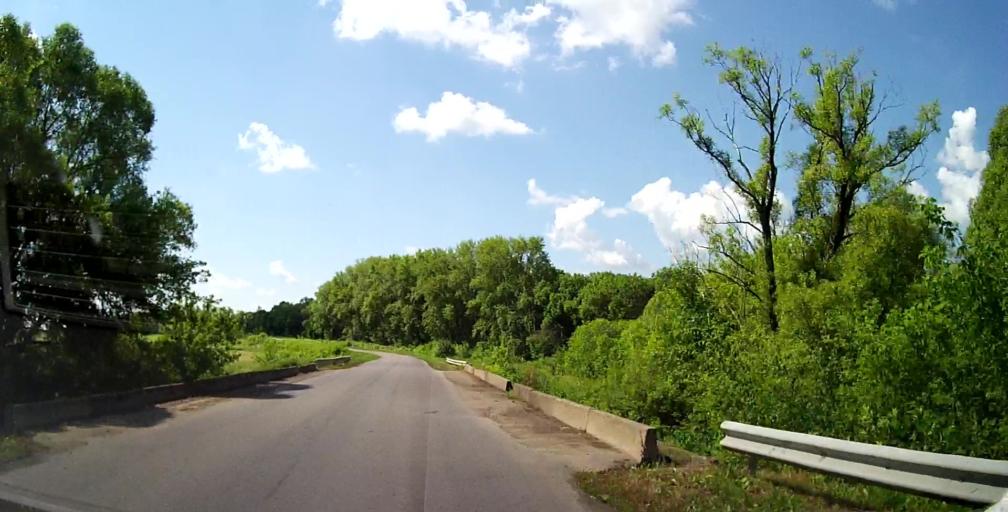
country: RU
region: Lipetsk
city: Chaplygin
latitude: 53.3045
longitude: 39.9522
